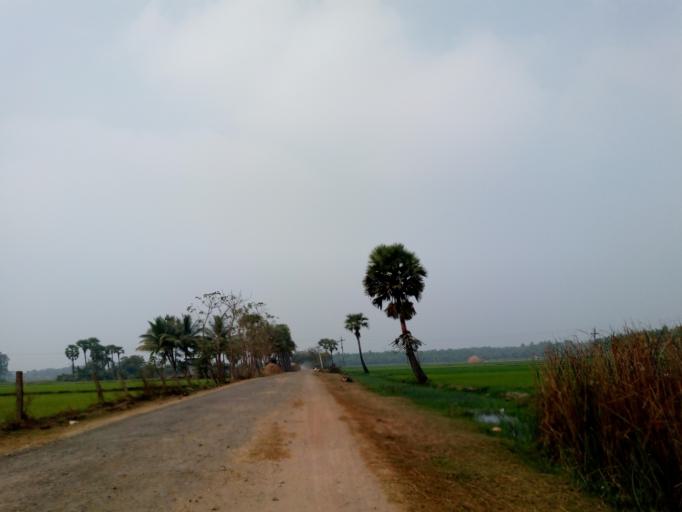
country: IN
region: Andhra Pradesh
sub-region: West Godavari
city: Tadepallegudem
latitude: 16.8644
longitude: 81.3108
